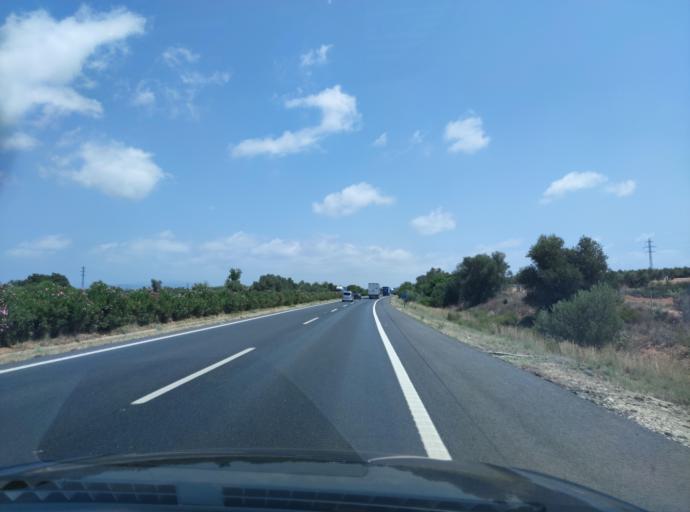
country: ES
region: Catalonia
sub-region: Provincia de Tarragona
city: Masdenverge
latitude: 40.6913
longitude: 0.5310
